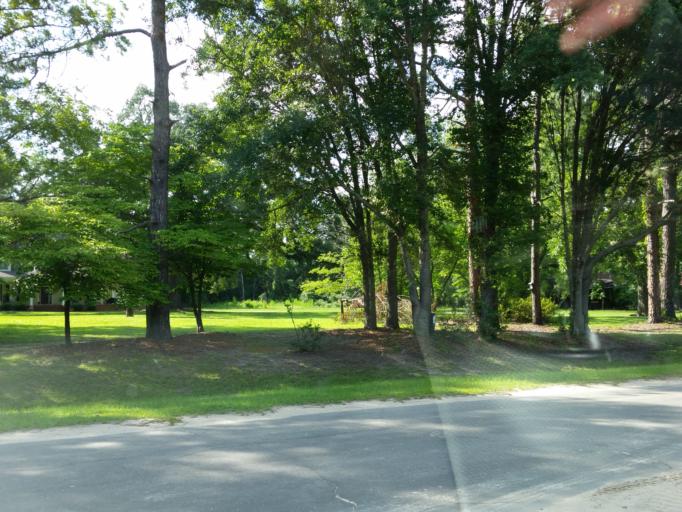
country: US
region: Georgia
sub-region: Lee County
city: Leesburg
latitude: 31.7822
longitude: -84.0190
